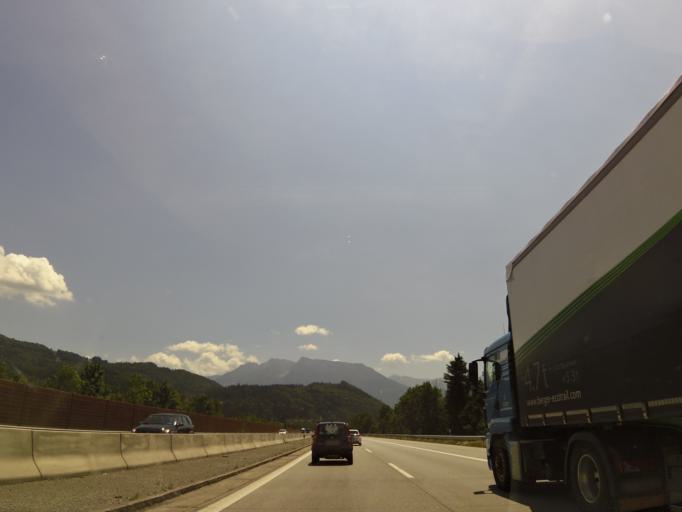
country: AT
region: Tyrol
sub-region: Politischer Bezirk Kufstein
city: Erl
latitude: 47.6746
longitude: 12.1723
